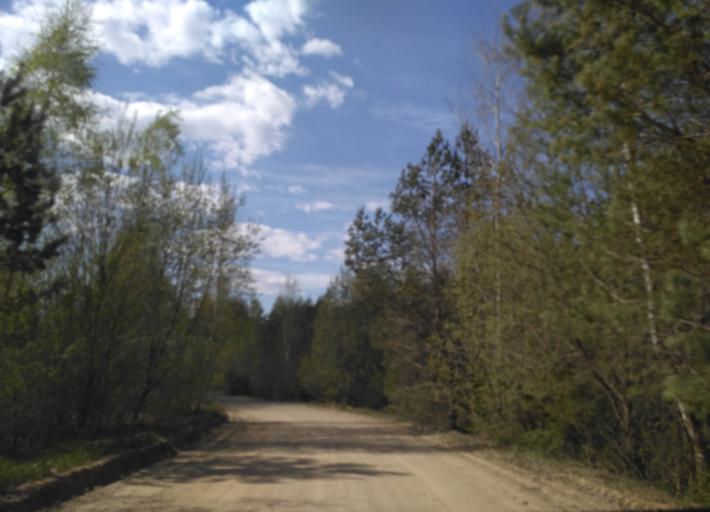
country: BY
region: Minsk
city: Narach
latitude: 54.9875
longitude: 26.6015
